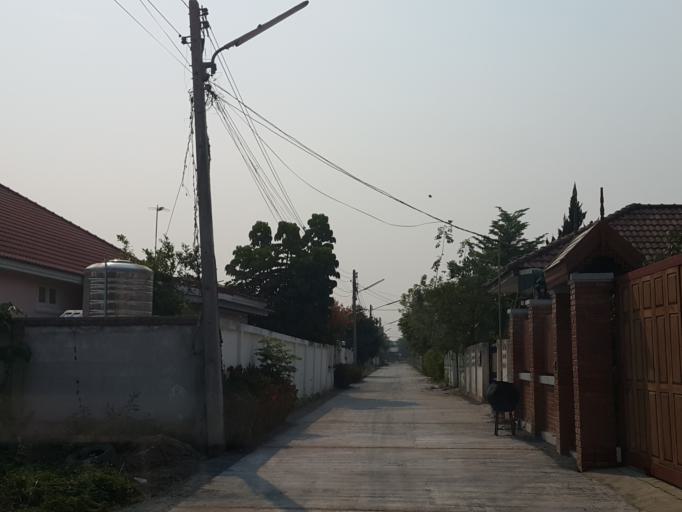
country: TH
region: Chiang Mai
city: San Kamphaeng
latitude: 18.7479
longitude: 99.0945
